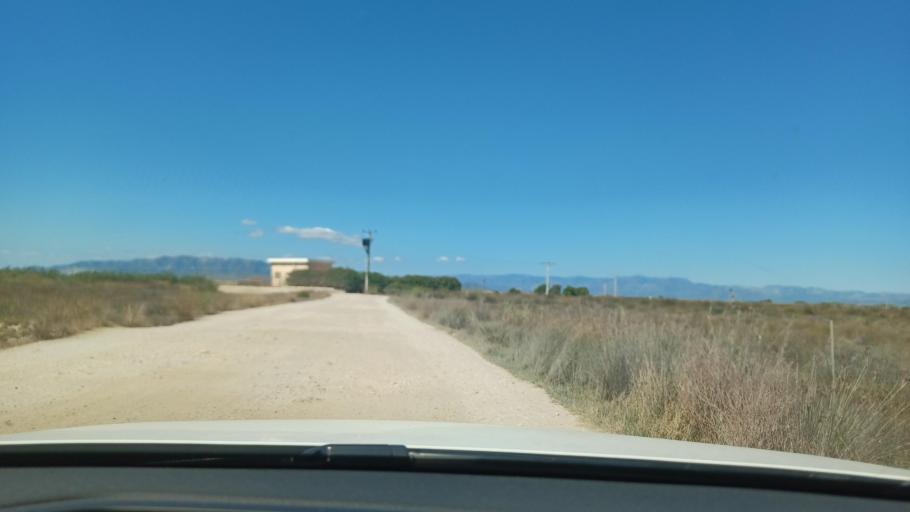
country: ES
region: Catalonia
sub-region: Provincia de Tarragona
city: Deltebre
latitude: 40.6483
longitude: 0.7654
